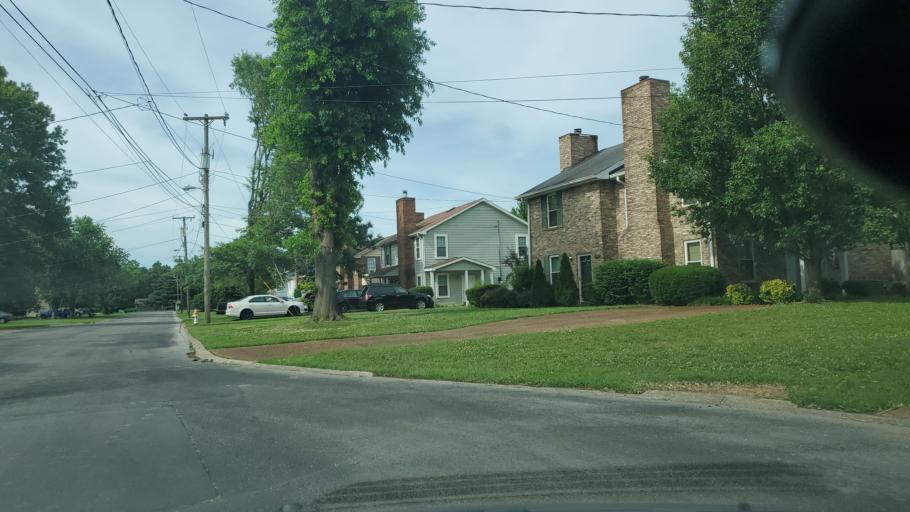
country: US
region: Tennessee
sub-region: Davidson County
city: Lakewood
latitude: 36.2065
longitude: -86.6877
